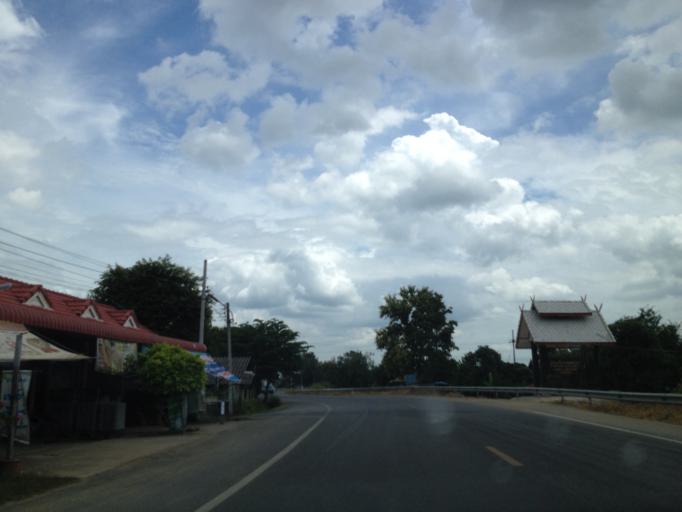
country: TH
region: Chiang Mai
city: San Pa Tong
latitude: 18.6336
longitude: 98.8624
